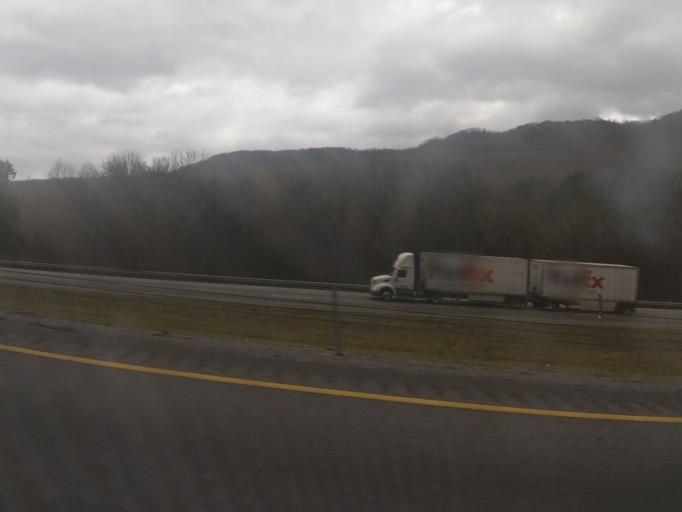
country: US
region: Tennessee
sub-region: Marion County
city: Jasper
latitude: 35.0118
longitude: -85.5327
